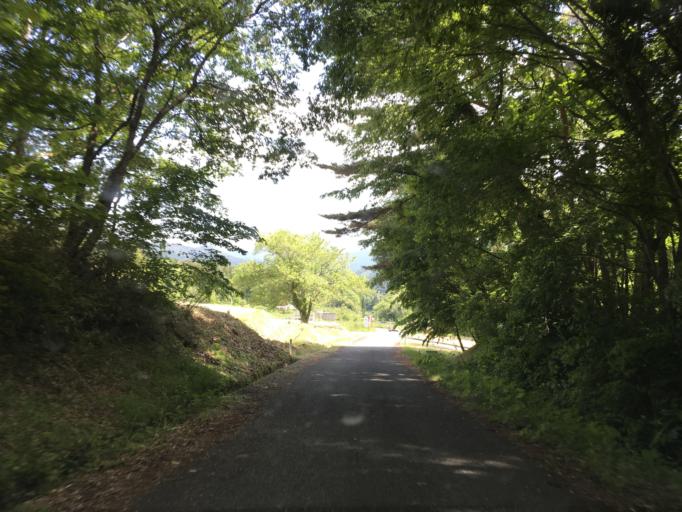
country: JP
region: Iwate
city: Ofunato
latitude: 38.9545
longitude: 141.4509
